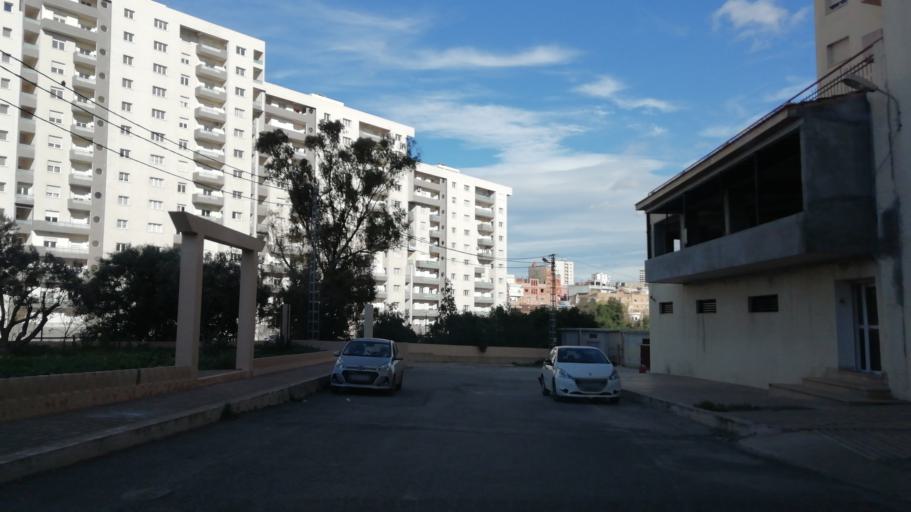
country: DZ
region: Oran
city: Oran
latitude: 35.7038
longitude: -0.6215
